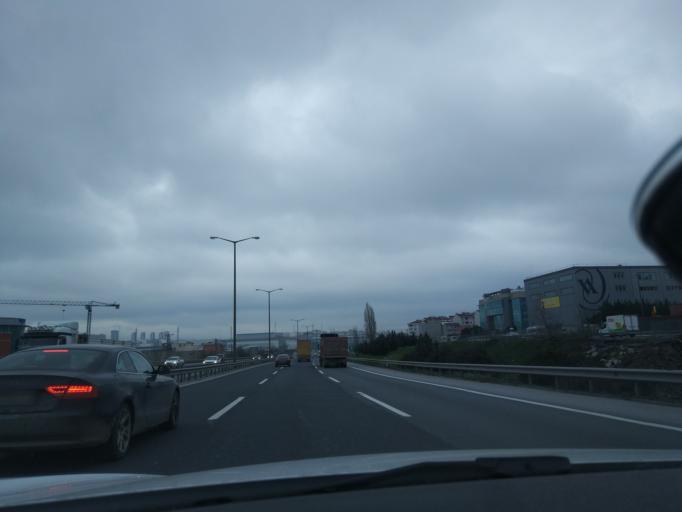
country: TR
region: Istanbul
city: Esenyurt
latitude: 41.0590
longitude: 28.6573
